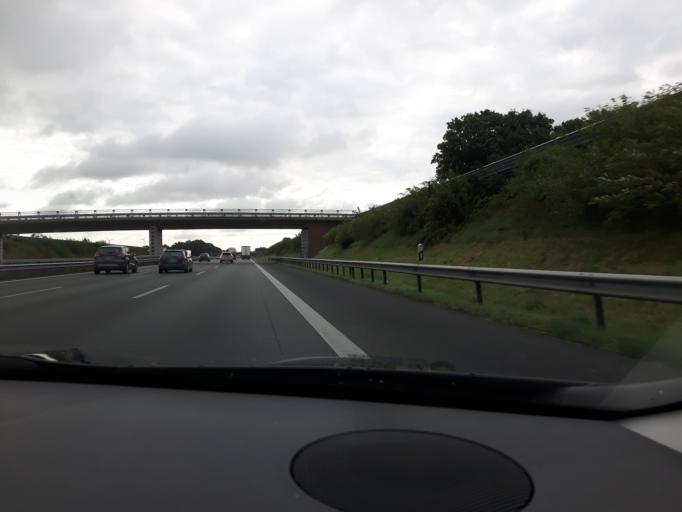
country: DE
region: Lower Saxony
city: Oyten
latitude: 53.0541
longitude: 9.0547
